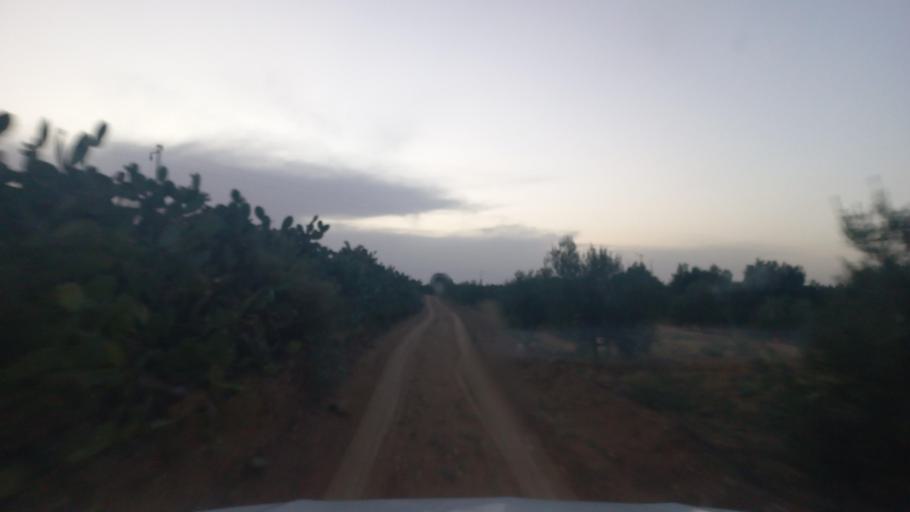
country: TN
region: Al Qasrayn
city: Kasserine
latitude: 35.2316
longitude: 9.0332
